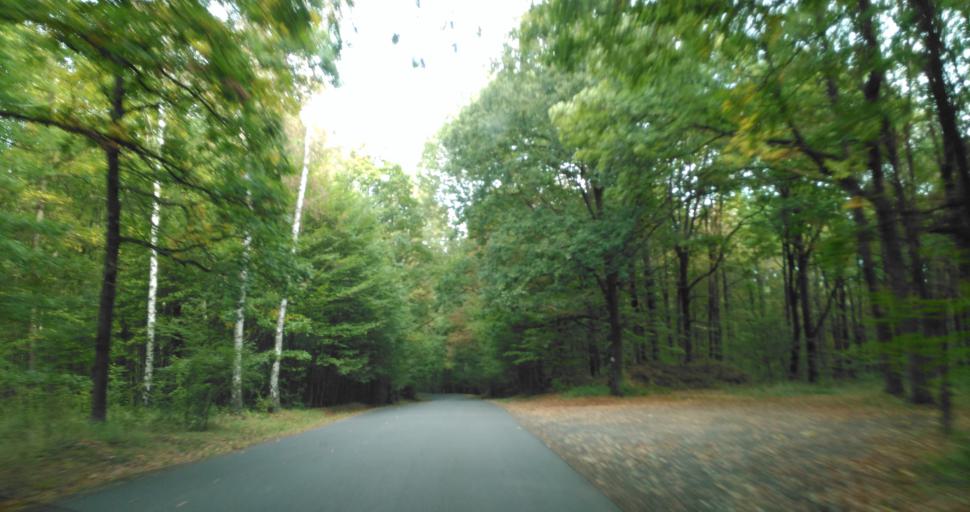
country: CZ
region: Plzensky
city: Zbiroh
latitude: 49.9463
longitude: 13.7640
